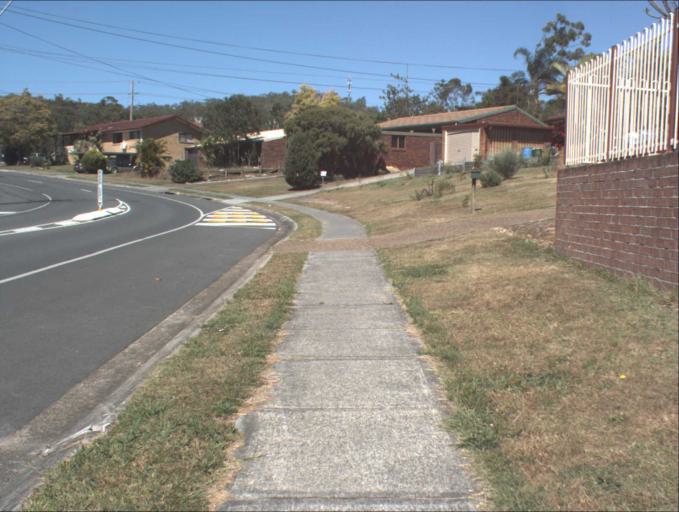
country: AU
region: Queensland
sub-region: Logan
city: Windaroo
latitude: -27.7245
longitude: 153.2053
